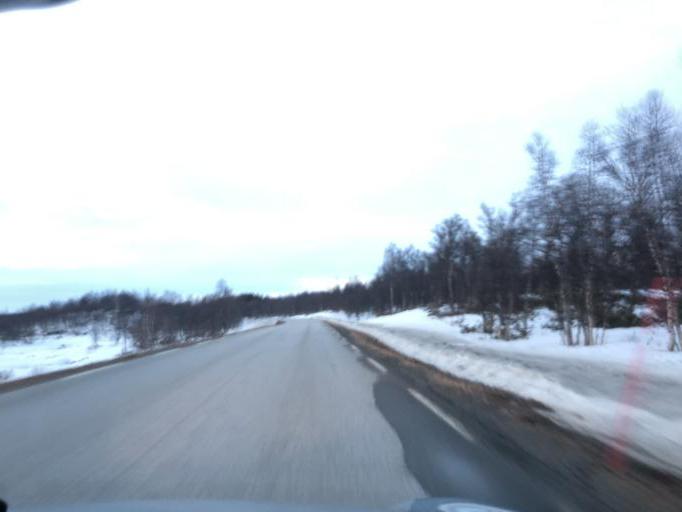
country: NO
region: Sor-Trondelag
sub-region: Tydal
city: Aas
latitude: 62.7142
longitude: 11.8152
